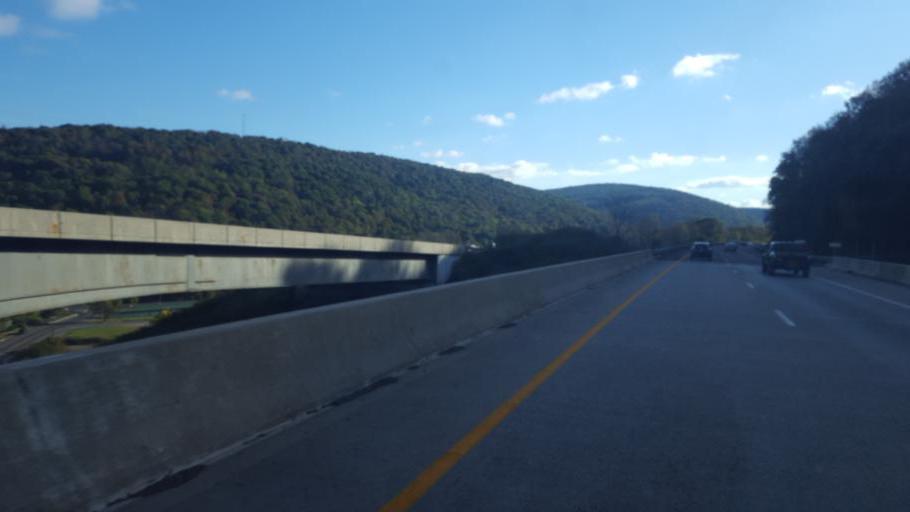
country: US
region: Maryland
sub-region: Allegany County
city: Frostburg
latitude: 39.6396
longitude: -78.8905
